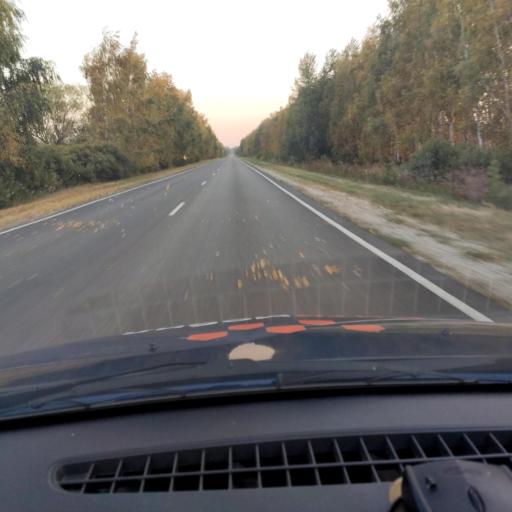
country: RU
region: Voronezj
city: Latnaya
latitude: 51.6333
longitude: 38.7832
